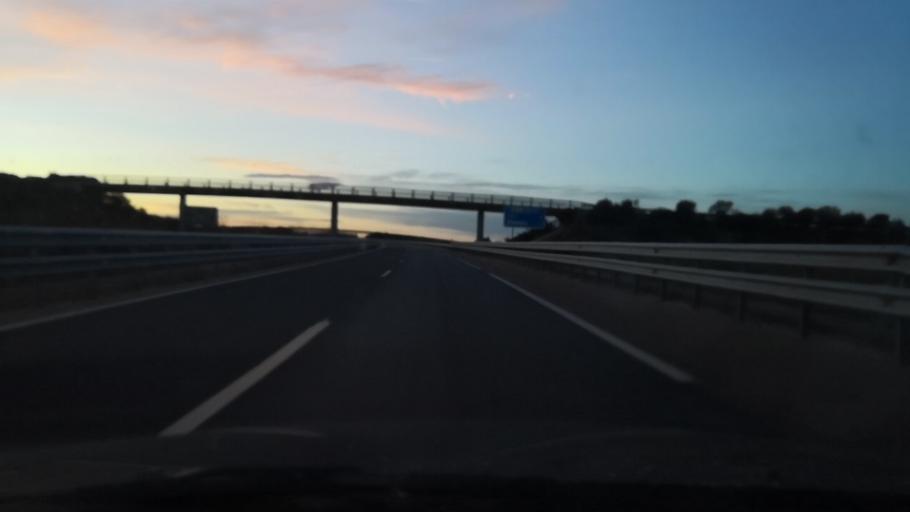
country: ES
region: Castille and Leon
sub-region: Provincia de Zamora
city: Morales de Toro
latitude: 41.5438
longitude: -5.2979
